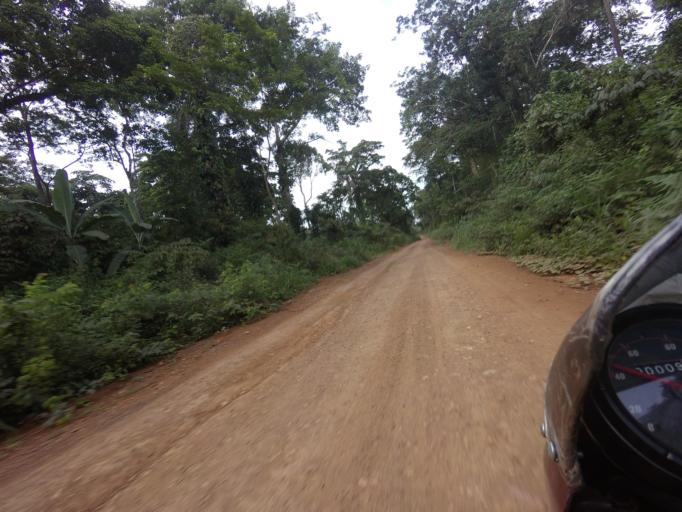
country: SL
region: Eastern Province
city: Kailahun
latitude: 8.2417
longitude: -10.6117
